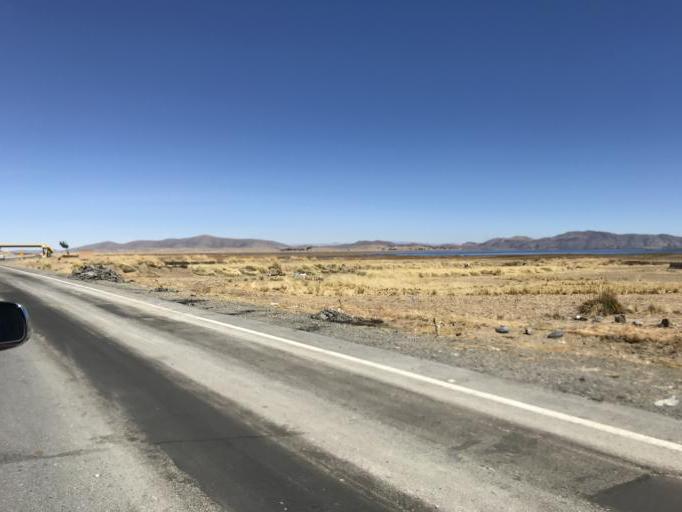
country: BO
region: La Paz
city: Huarina
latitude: -16.2346
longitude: -68.5777
